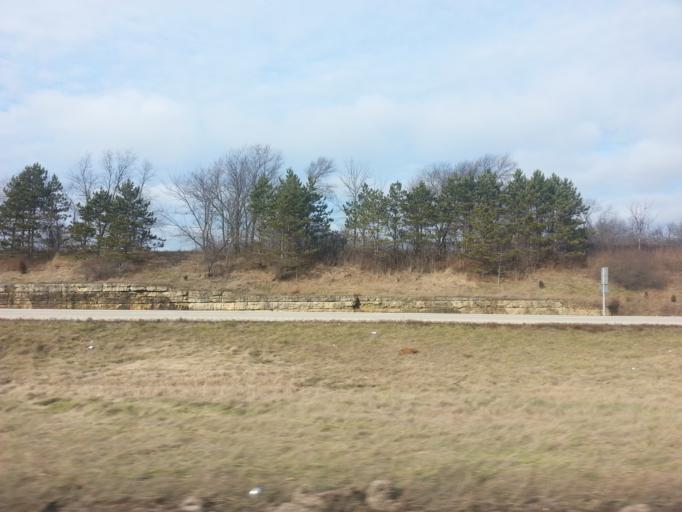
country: US
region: Illinois
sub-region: Winnebago County
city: Cherry Valley
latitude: 42.2025
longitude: -89.0182
